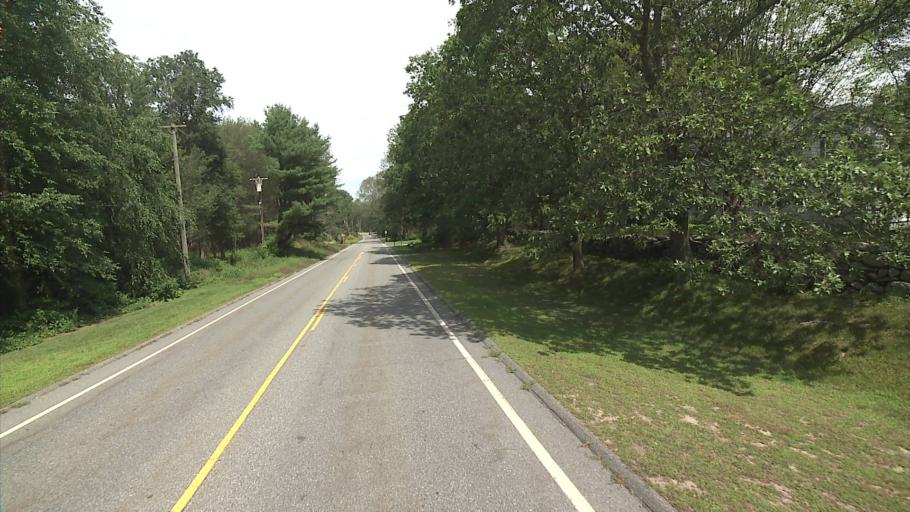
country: US
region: Connecticut
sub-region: Windham County
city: Putnam
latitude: 41.9037
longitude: -71.8665
